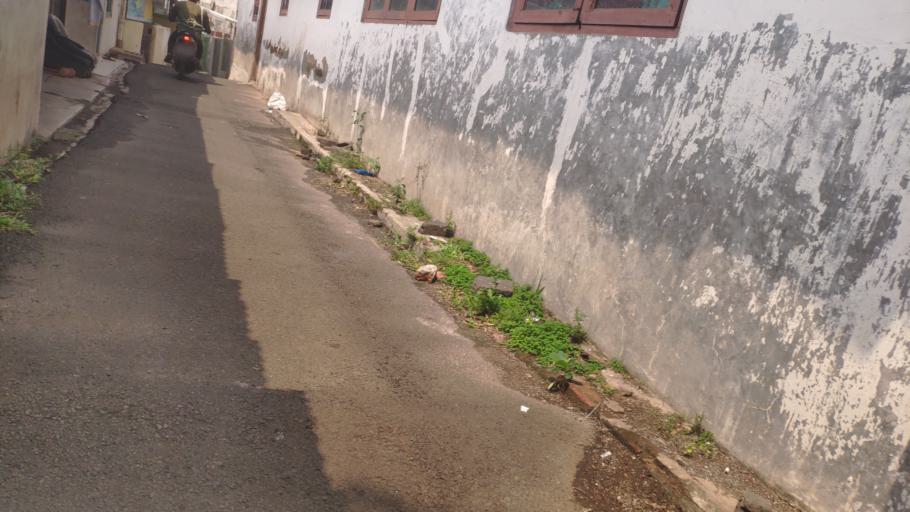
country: ID
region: Jakarta Raya
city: Jakarta
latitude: -6.2684
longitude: 106.8304
